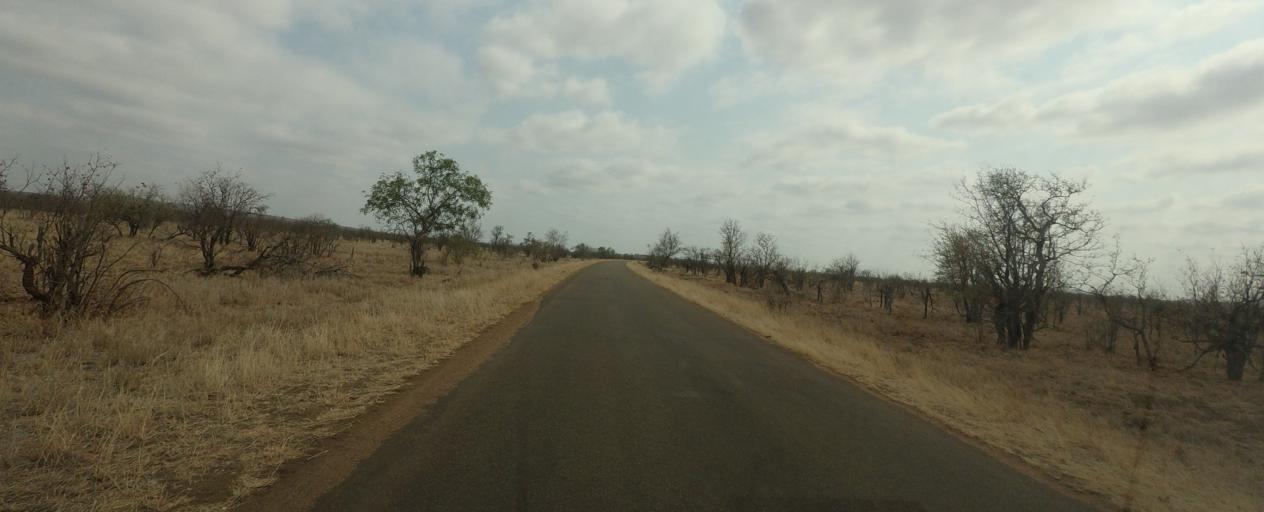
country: ZA
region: Limpopo
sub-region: Vhembe District Municipality
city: Mutale
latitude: -22.6127
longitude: 31.1737
